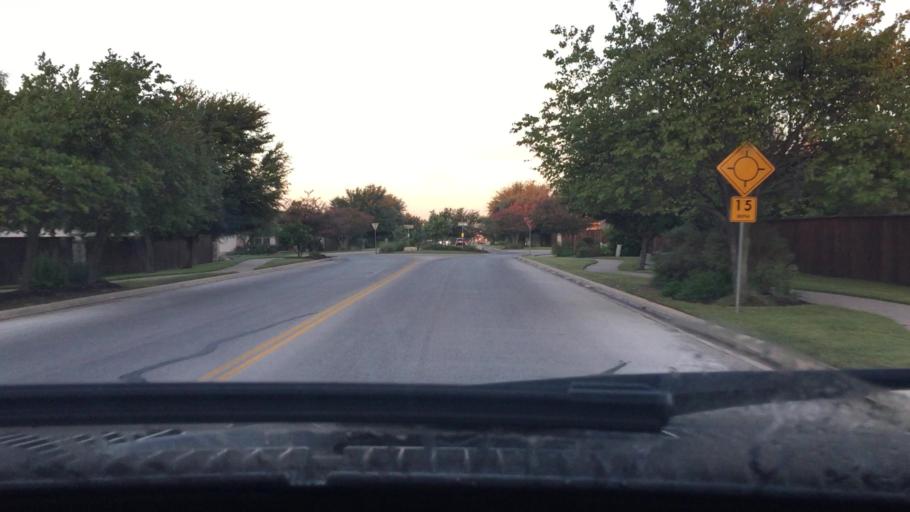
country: US
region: Texas
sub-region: Williamson County
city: Leander
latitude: 30.5398
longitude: -97.8566
